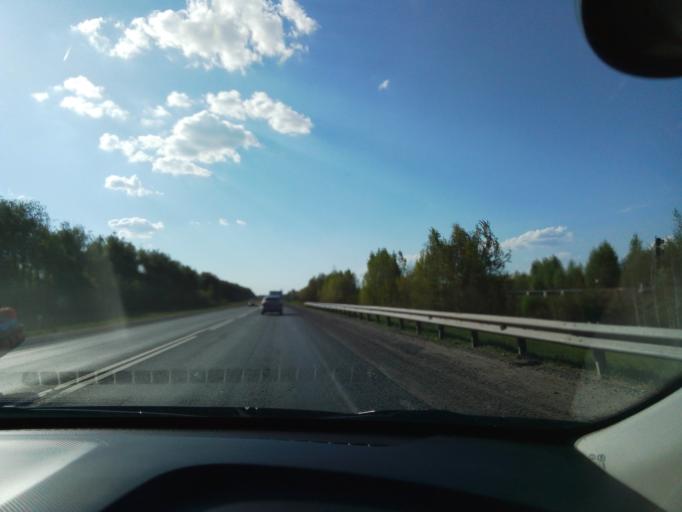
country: RU
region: Chuvashia
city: Kugesi
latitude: 56.0546
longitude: 47.2735
